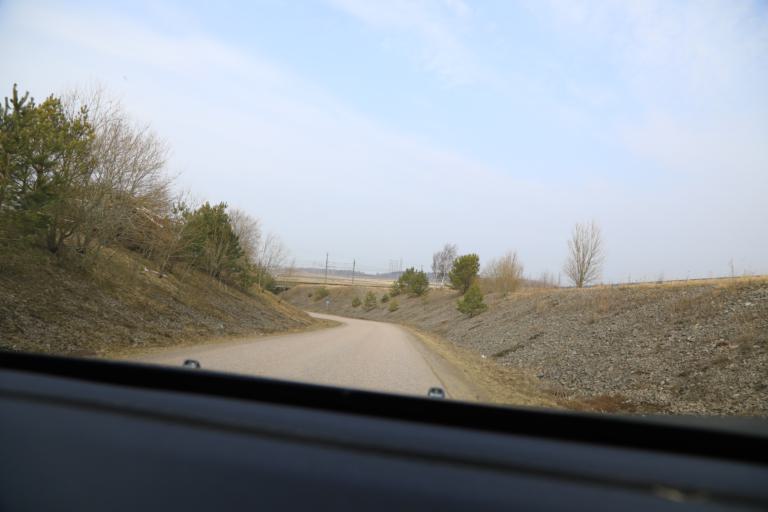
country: SE
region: Halland
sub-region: Kungsbacka Kommun
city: Frillesas
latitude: 57.2676
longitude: 12.1738
